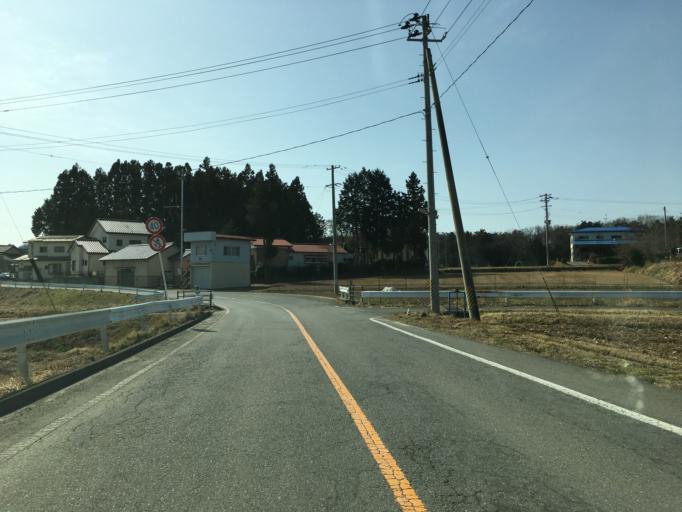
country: JP
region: Fukushima
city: Motomiya
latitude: 37.5460
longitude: 140.3595
